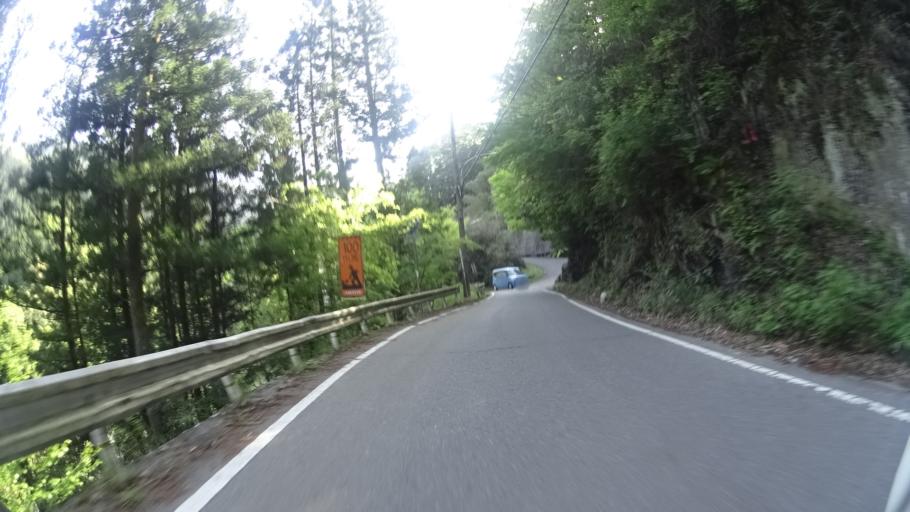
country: JP
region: Tokushima
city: Ikedacho
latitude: 33.8660
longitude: 133.9603
